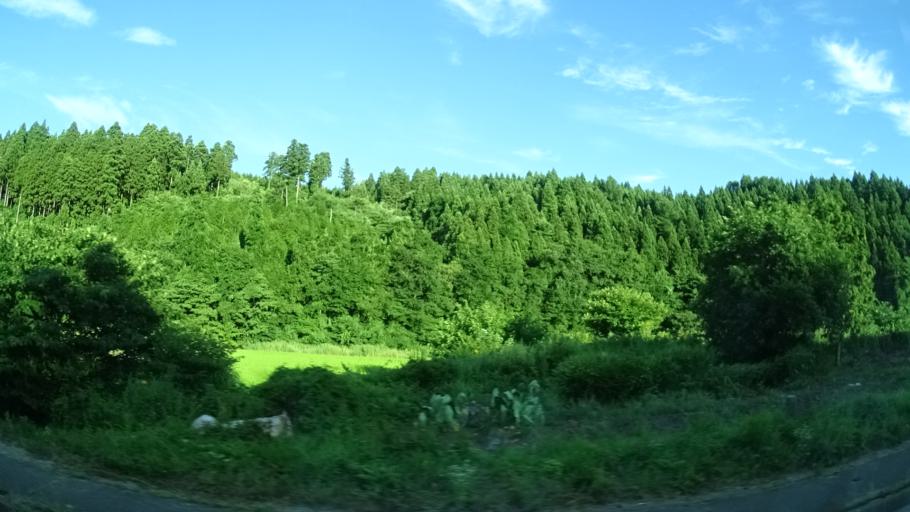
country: JP
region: Ishikawa
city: Nanao
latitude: 37.3045
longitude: 136.8994
